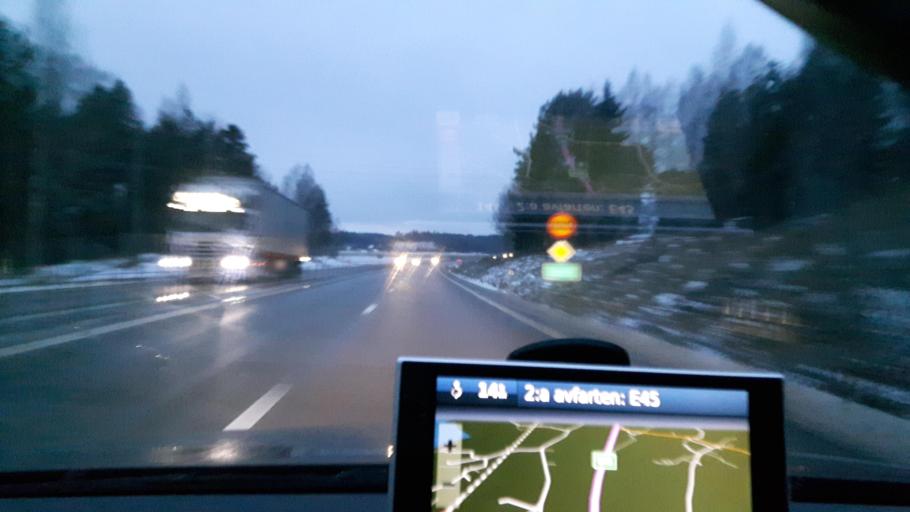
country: SE
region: Vaermland
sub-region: Saffle Kommun
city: Saeffle
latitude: 59.1212
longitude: 12.8547
